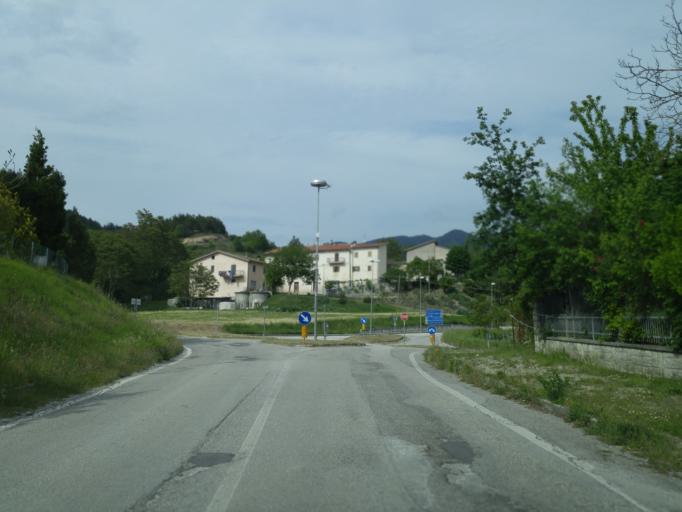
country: IT
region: The Marches
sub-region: Provincia di Pesaro e Urbino
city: Acqualagna
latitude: 43.6274
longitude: 12.6742
